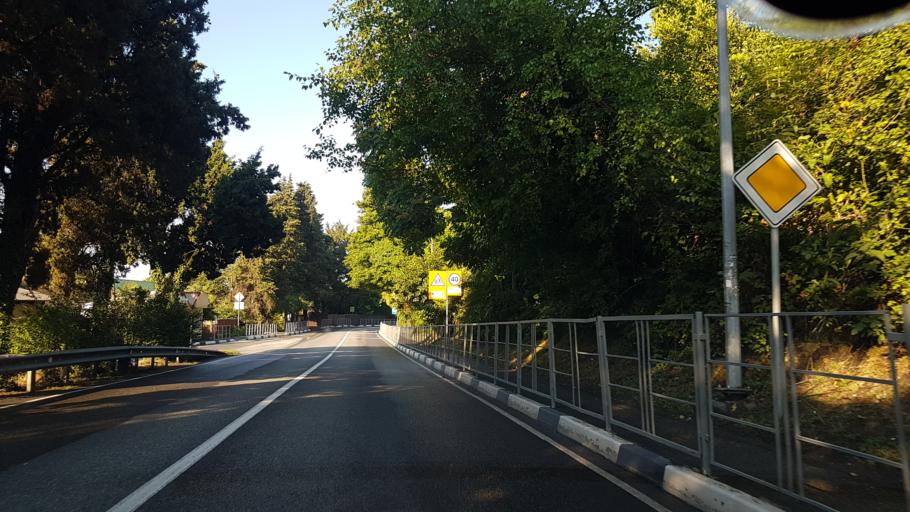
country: RU
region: Krasnodarskiy
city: Vardane
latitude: 43.7997
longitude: 39.4684
